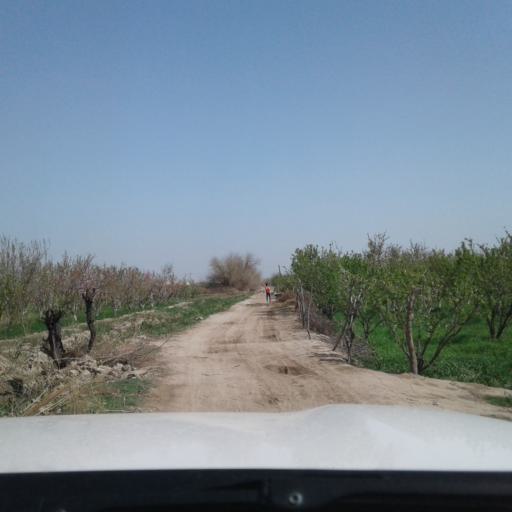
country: TM
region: Lebap
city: Turkmenabat
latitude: 38.9565
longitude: 63.6443
